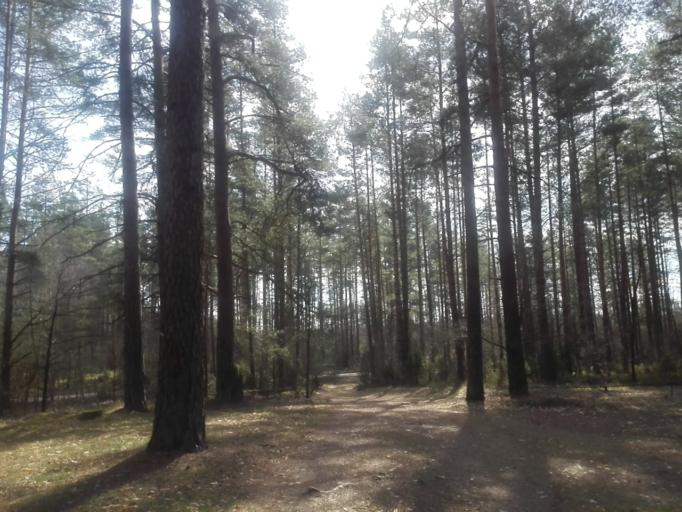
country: PL
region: Podlasie
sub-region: Powiat sejnenski
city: Sejny
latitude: 54.0279
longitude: 23.4119
